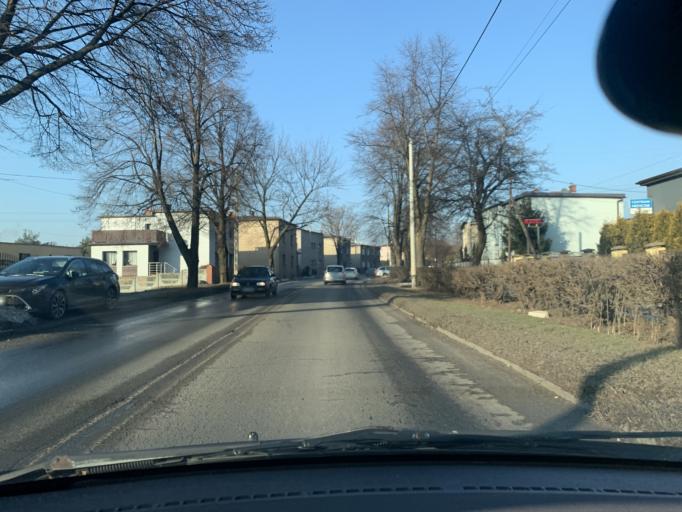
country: PL
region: Silesian Voivodeship
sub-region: Powiat tarnogorski
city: Radzionkow
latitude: 50.3917
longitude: 18.8977
